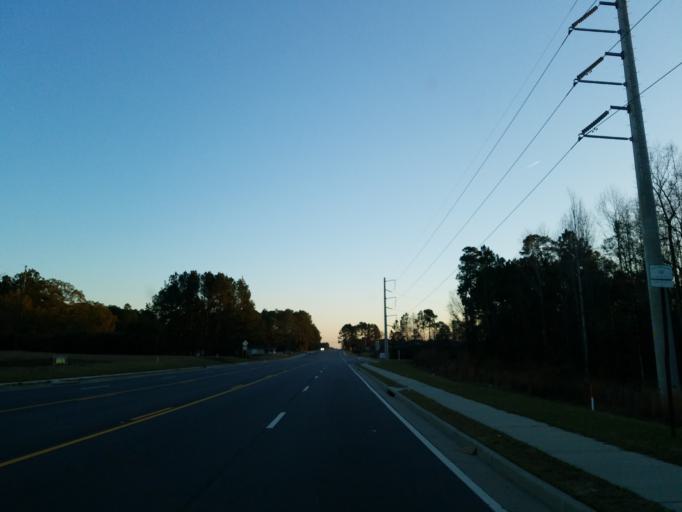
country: US
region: Georgia
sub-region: Tift County
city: Tifton
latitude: 31.4670
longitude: -83.5465
